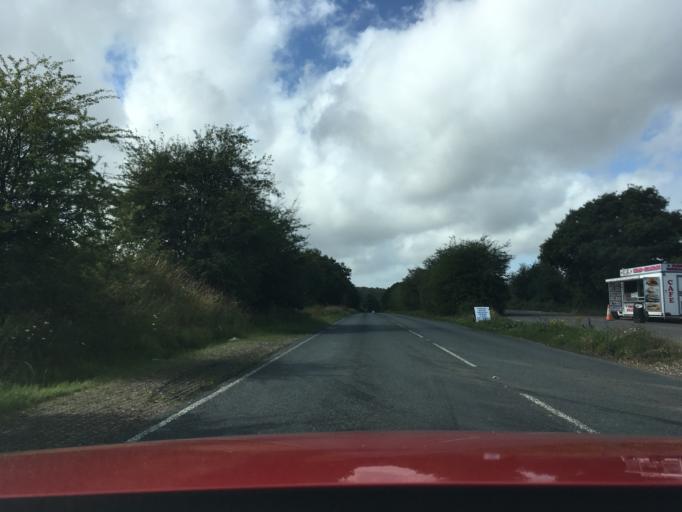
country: GB
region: England
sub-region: Hampshire
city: Overton
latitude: 51.2106
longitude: -1.1785
